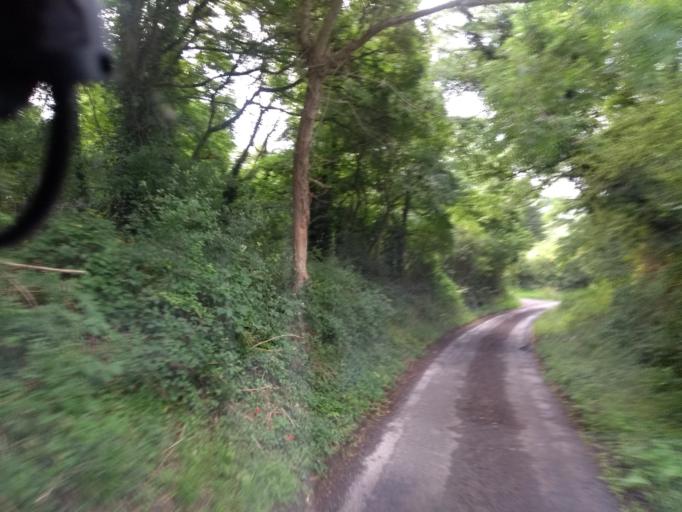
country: GB
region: England
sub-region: Somerset
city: Castle Cary
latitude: 51.0270
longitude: -2.5787
